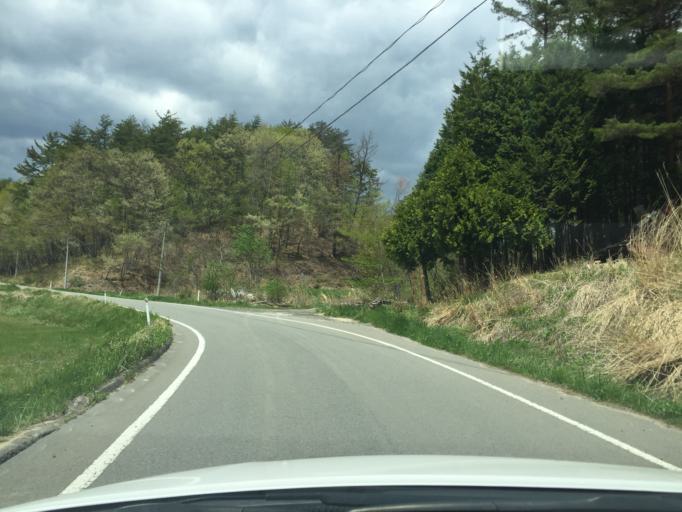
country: JP
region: Fukushima
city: Yanagawamachi-saiwaicho
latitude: 37.6966
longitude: 140.6758
